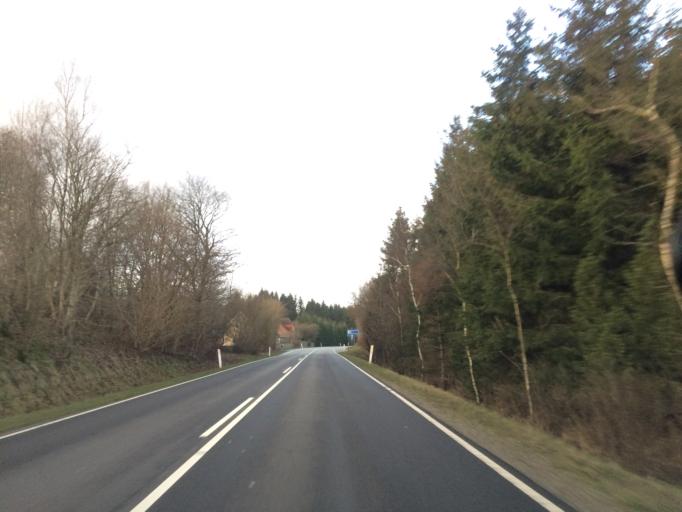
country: DK
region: Central Jutland
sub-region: Silkeborg Kommune
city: Svejbaek
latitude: 56.0959
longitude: 9.6513
